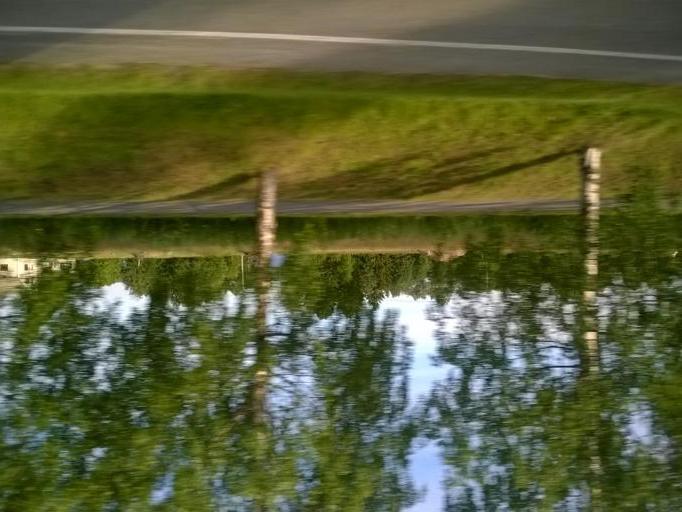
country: FI
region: Kainuu
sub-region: Kajaani
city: Sotkamo
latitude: 64.1261
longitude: 28.4193
